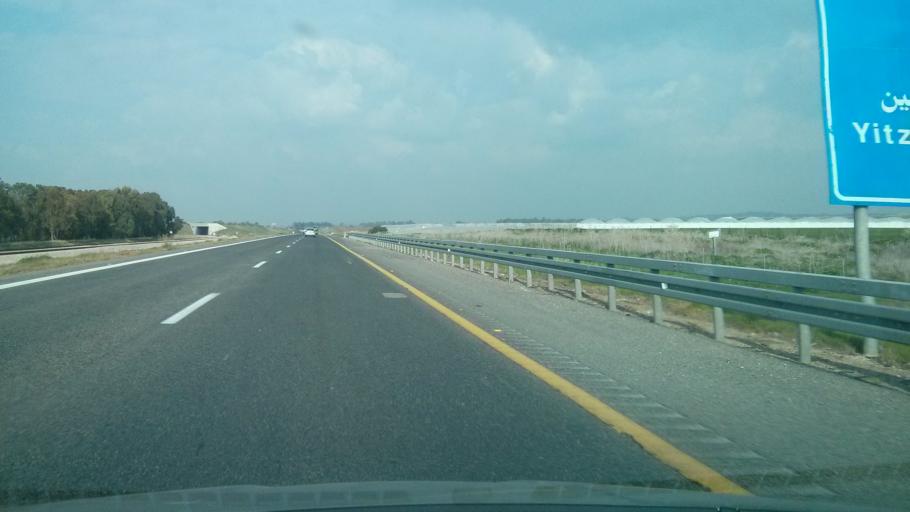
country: IL
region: Central District
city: Mazkeret Batya
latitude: 31.8192
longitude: 34.8449
